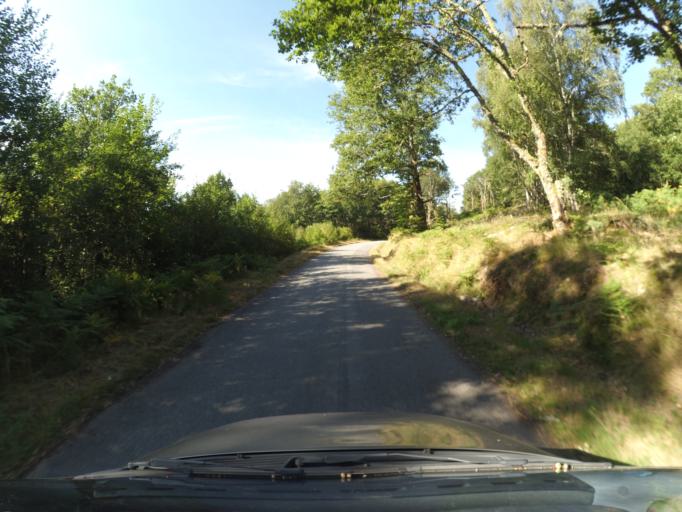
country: FR
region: Limousin
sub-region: Departement de la Correze
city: Bugeat
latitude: 45.6950
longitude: 1.9787
